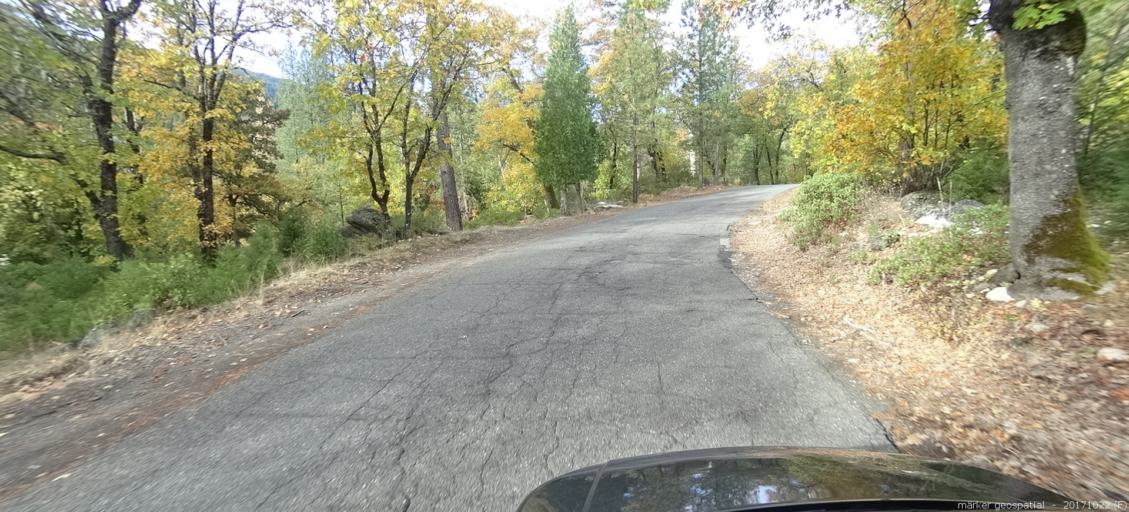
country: US
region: California
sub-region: Siskiyou County
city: Dunsmuir
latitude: 41.1555
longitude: -122.3480
